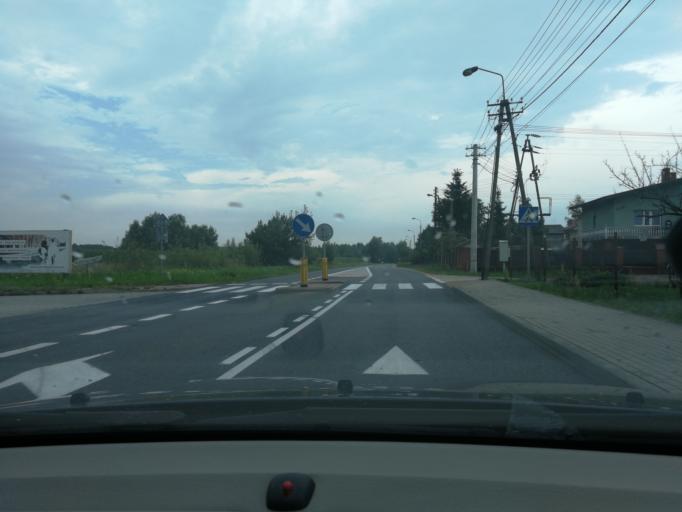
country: PL
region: Masovian Voivodeship
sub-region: Powiat zyrardowski
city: Radziejowice
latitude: 52.0088
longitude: 20.5584
